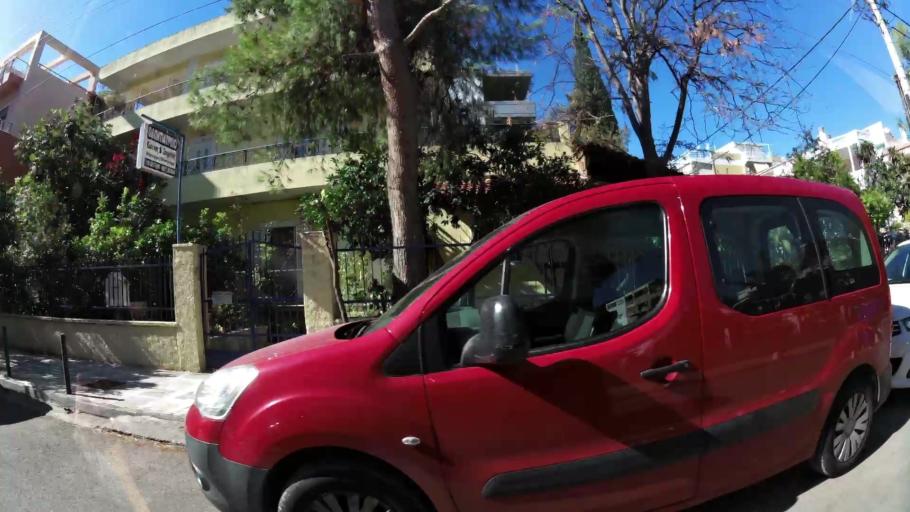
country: GR
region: Attica
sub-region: Nomarchia Athinas
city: Khalandrion
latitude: 38.0234
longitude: 23.8133
